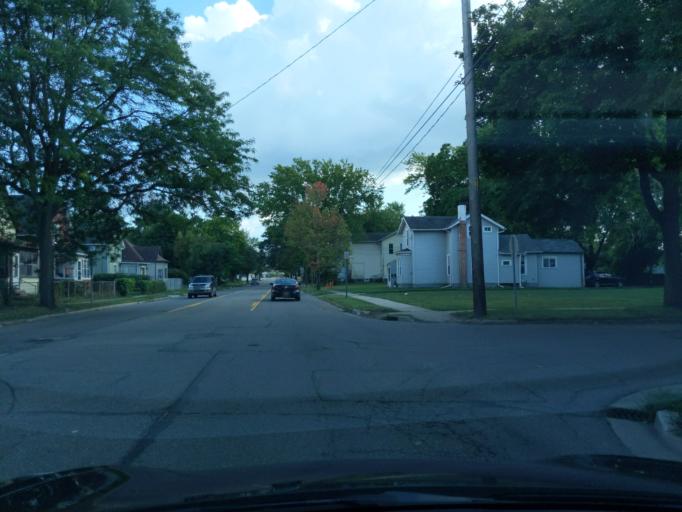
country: US
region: Michigan
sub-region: Jackson County
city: Jackson
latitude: 42.2520
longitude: -84.4019
